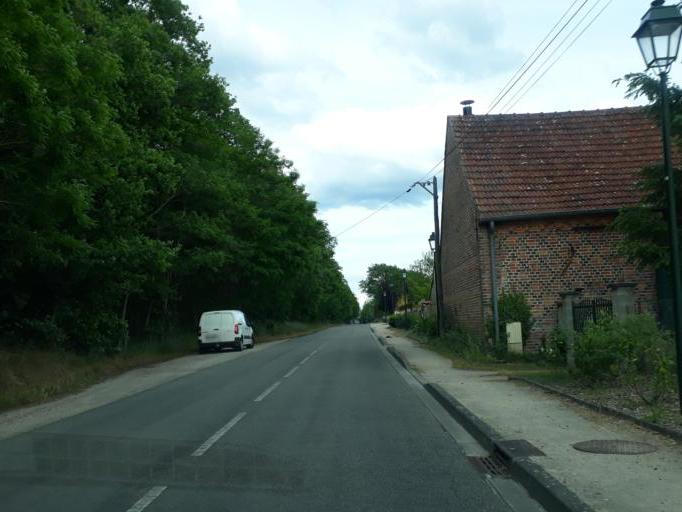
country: FR
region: Centre
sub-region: Departement du Loiret
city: La Ferte-Saint-Aubin
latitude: 47.7243
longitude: 1.9555
